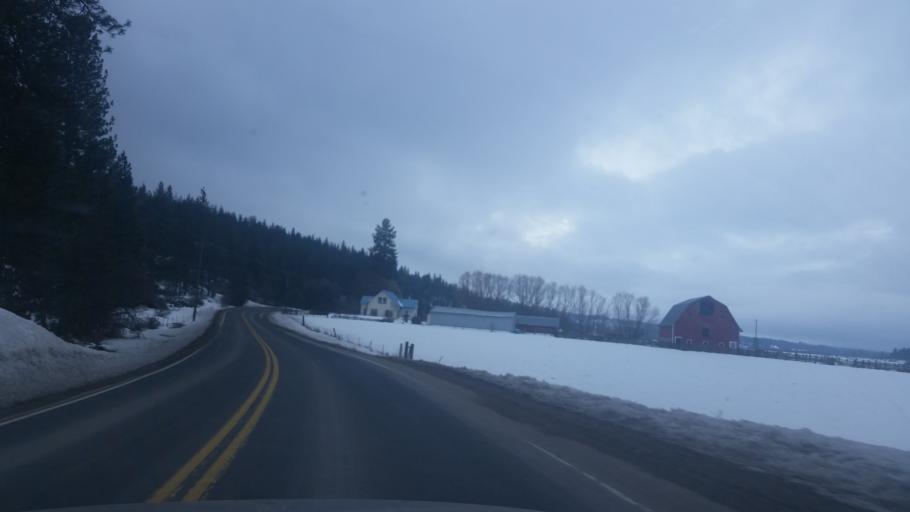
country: US
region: Washington
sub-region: Spokane County
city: Deer Park
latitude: 47.9389
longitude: -117.7705
